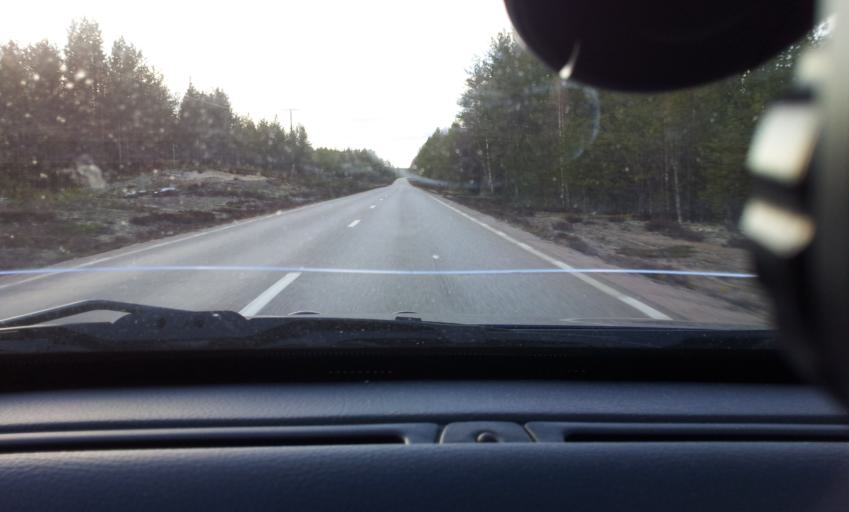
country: SE
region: Vaesternorrland
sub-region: Ange Kommun
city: Ange
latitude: 62.0952
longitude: 15.0834
